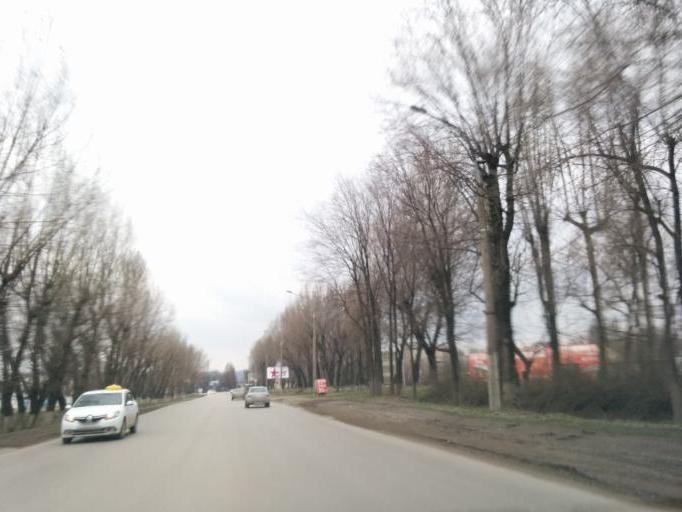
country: RU
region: Rostov
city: Novocherkassk
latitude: 47.4675
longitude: 40.1002
